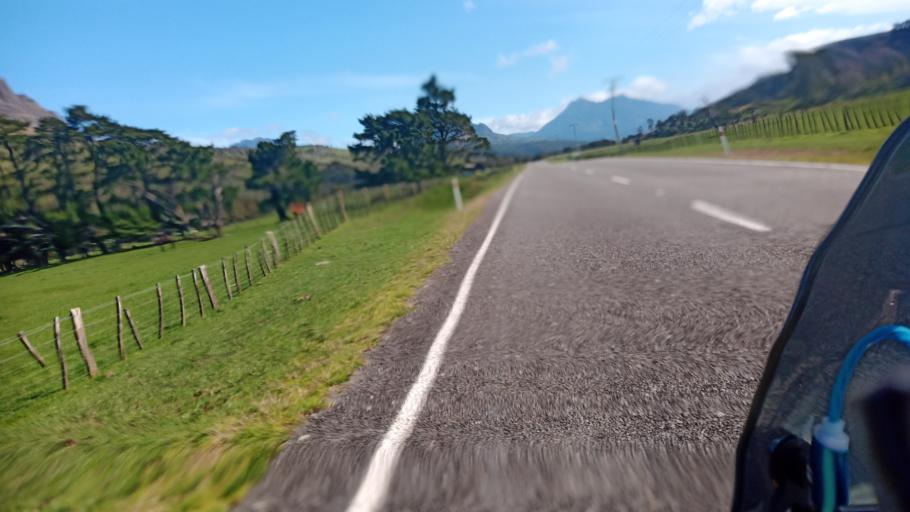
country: NZ
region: Gisborne
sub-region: Gisborne District
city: Gisborne
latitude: -37.8659
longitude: 178.2110
